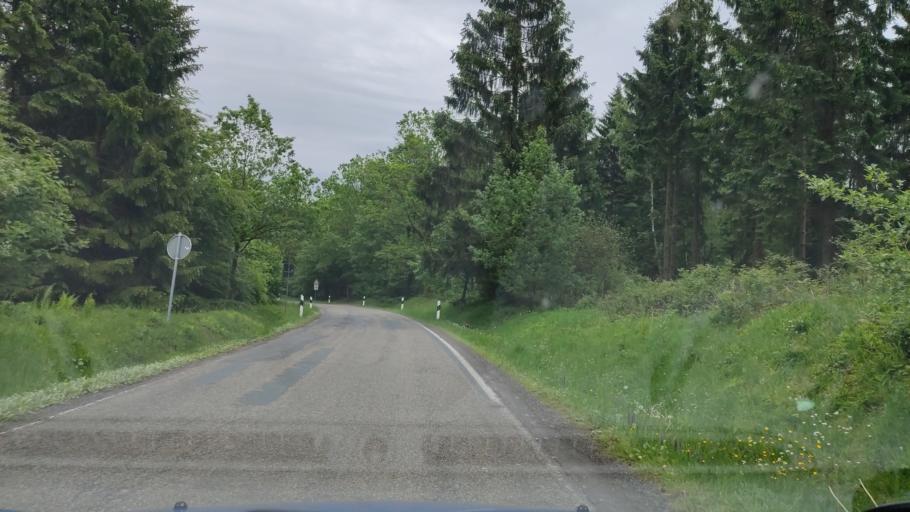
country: DE
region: Lower Saxony
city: Hardegsen
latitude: 51.7086
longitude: 9.7532
